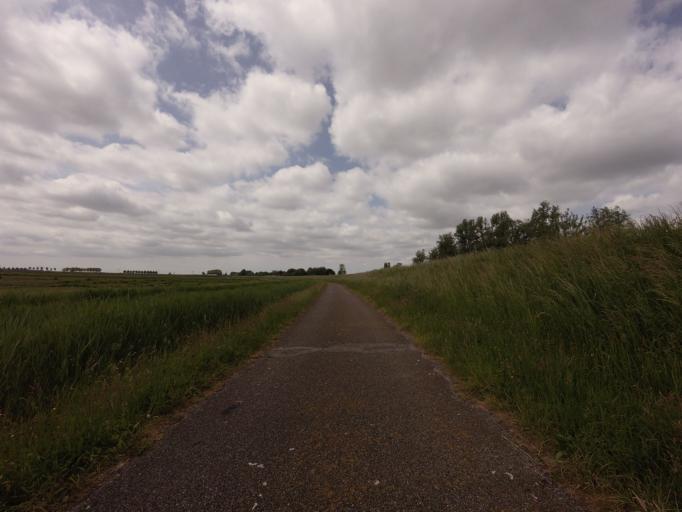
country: NL
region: North Holland
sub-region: Gemeente Hoorn
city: Hoorn
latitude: 52.6011
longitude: 5.0172
